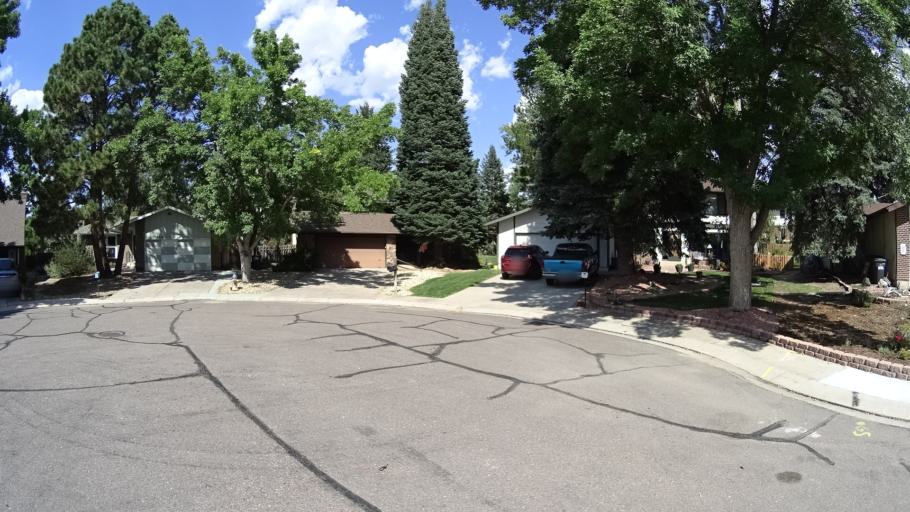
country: US
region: Colorado
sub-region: El Paso County
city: Cimarron Hills
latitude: 38.8750
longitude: -104.7463
